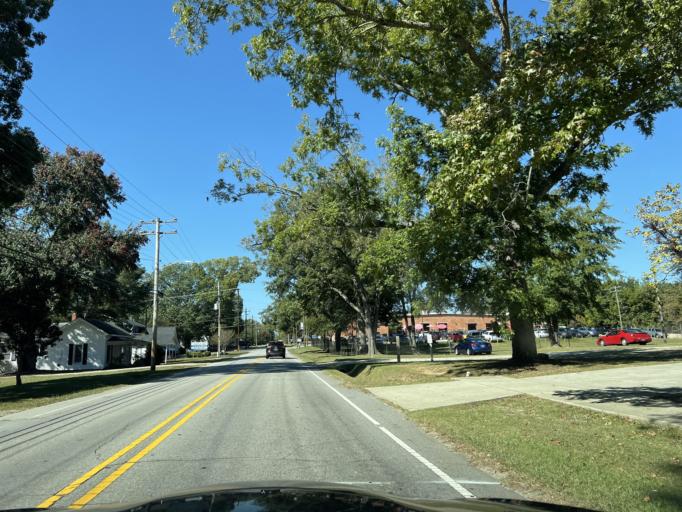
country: US
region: North Carolina
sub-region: Johnston County
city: Clayton
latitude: 35.6580
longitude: -78.4658
